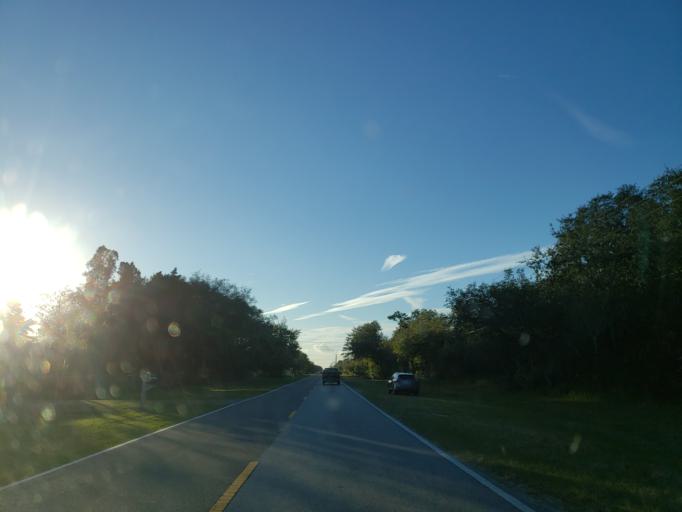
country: US
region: Florida
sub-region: Hillsborough County
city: Riverview
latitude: 27.8215
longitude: -82.2915
